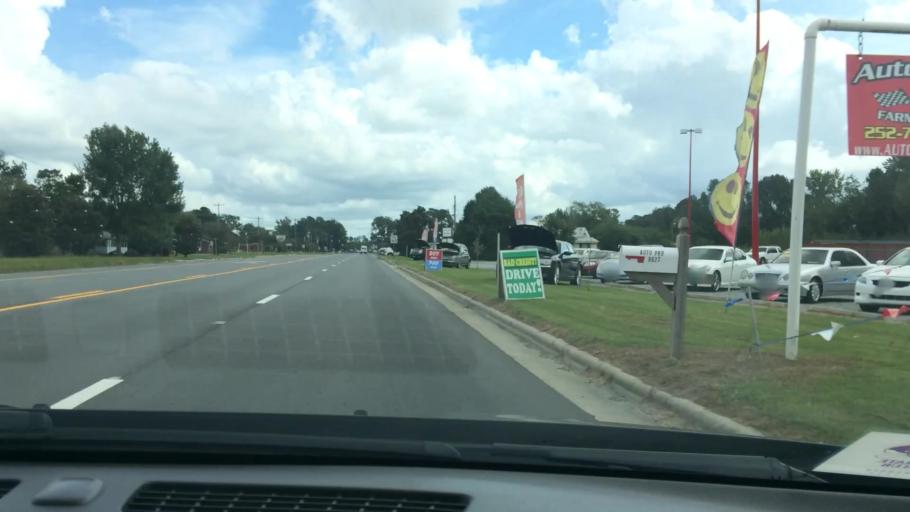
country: US
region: North Carolina
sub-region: Pitt County
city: Farmville
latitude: 35.5835
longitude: -77.5978
